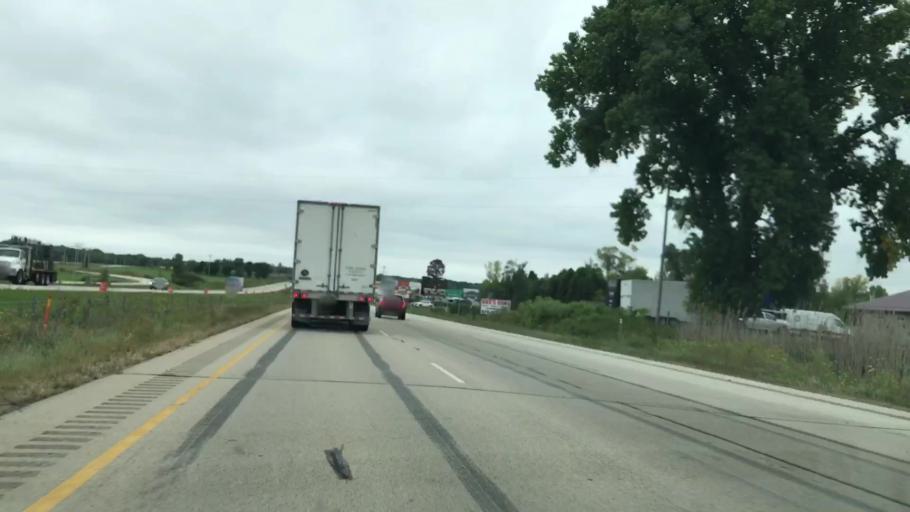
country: US
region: Wisconsin
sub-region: Brown County
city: Suamico
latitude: 44.6711
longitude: -88.0504
